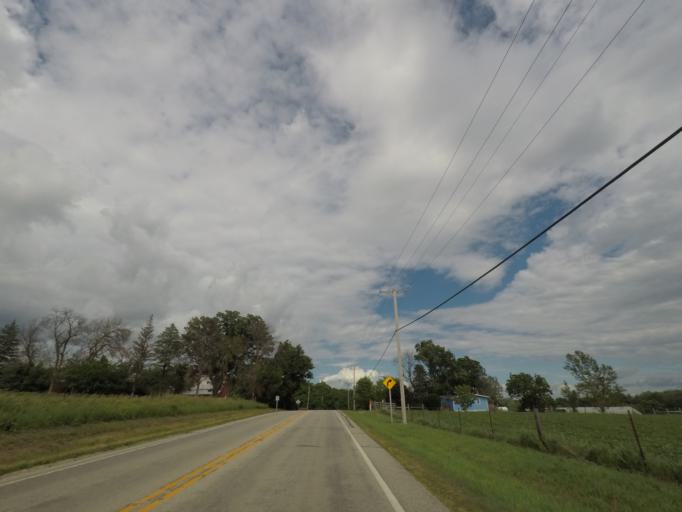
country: US
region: Wisconsin
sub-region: Dane County
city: Belleville
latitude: 42.8282
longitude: -89.5177
